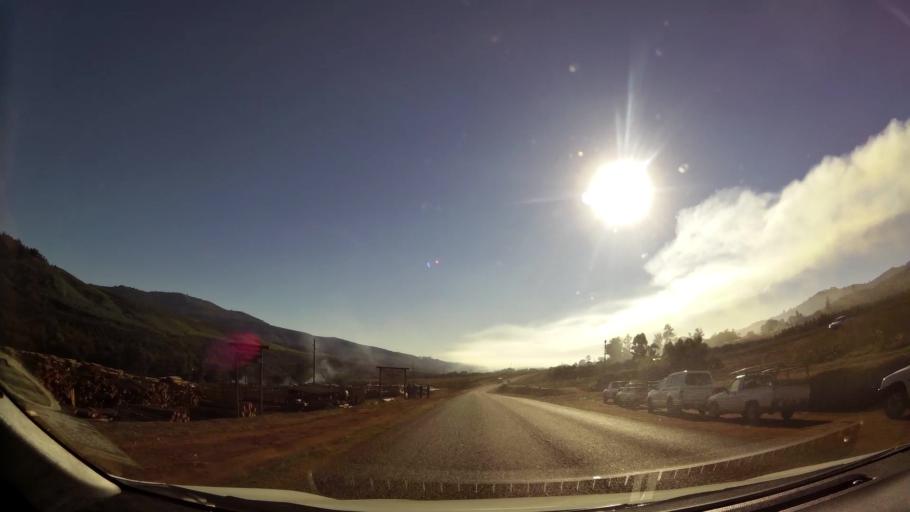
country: ZA
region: Limpopo
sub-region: Mopani District Municipality
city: Tzaneen
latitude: -23.9072
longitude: 30.0615
